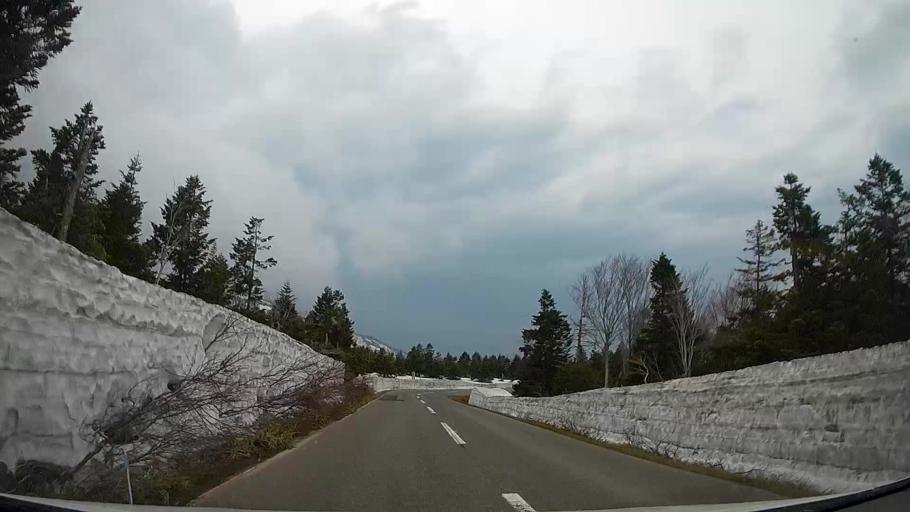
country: JP
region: Aomori
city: Aomori Shi
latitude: 40.6383
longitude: 140.8648
